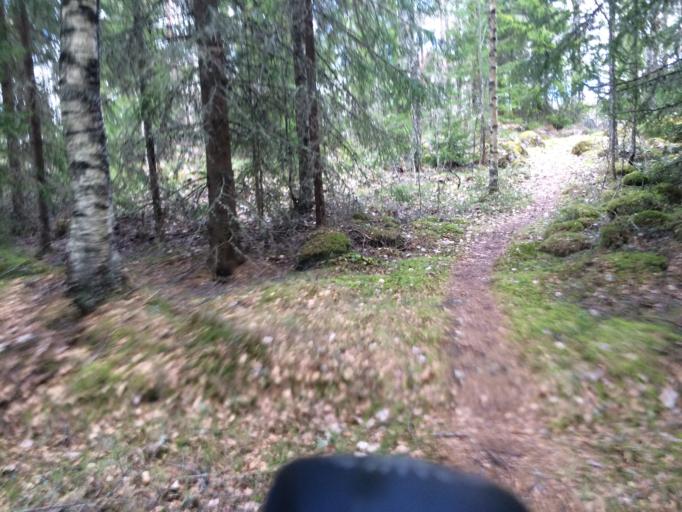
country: SE
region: OErebro
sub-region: Hallefors Kommun
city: Haellefors
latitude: 60.0407
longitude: 14.5252
